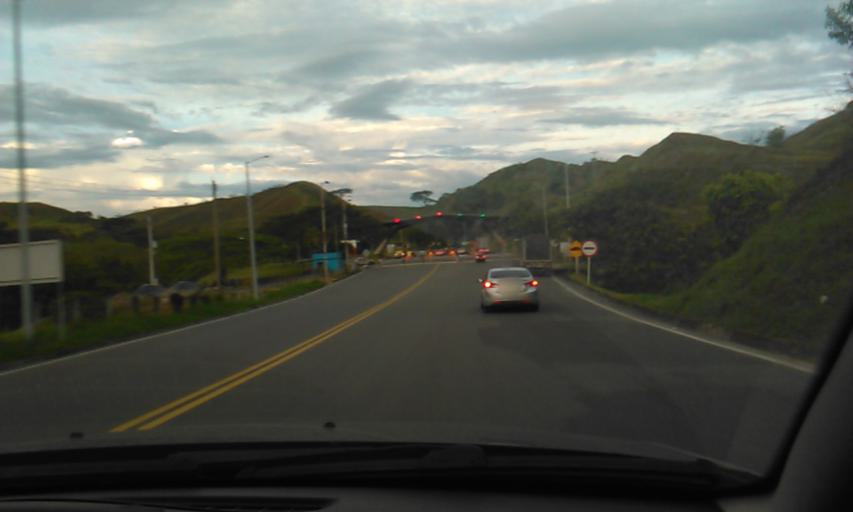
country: CO
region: Valle del Cauca
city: Caicedonia
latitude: 4.4070
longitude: -75.9008
